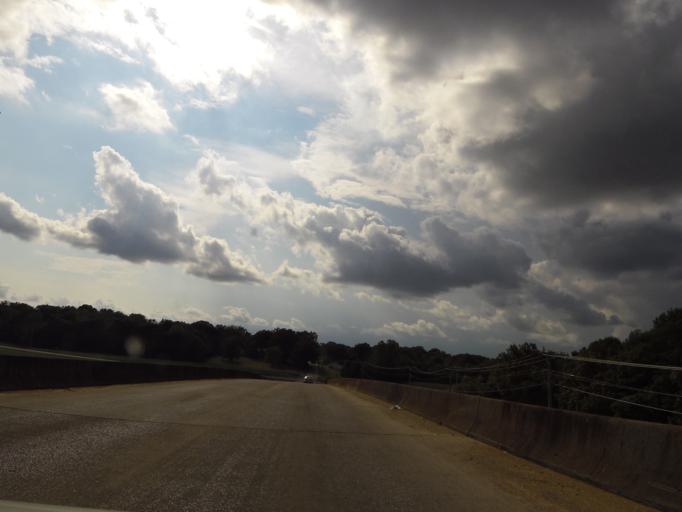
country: US
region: Mississippi
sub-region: Alcorn County
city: Corinth
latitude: 34.9455
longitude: -88.5250
